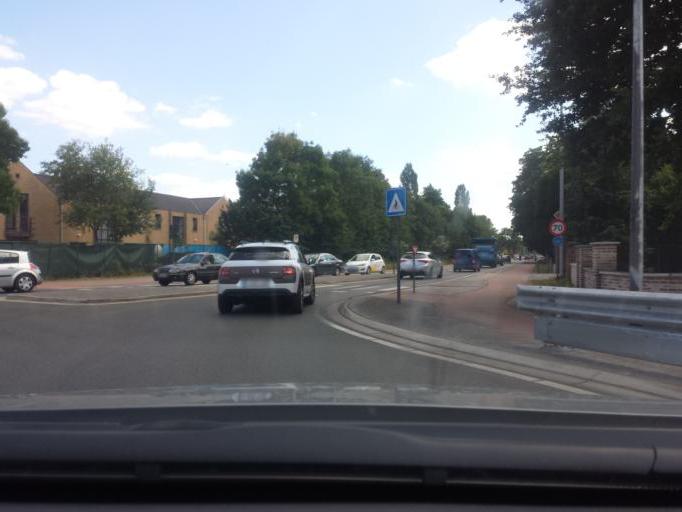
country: BE
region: Flanders
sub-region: Provincie Limburg
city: Beringen
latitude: 51.0640
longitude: 5.2216
